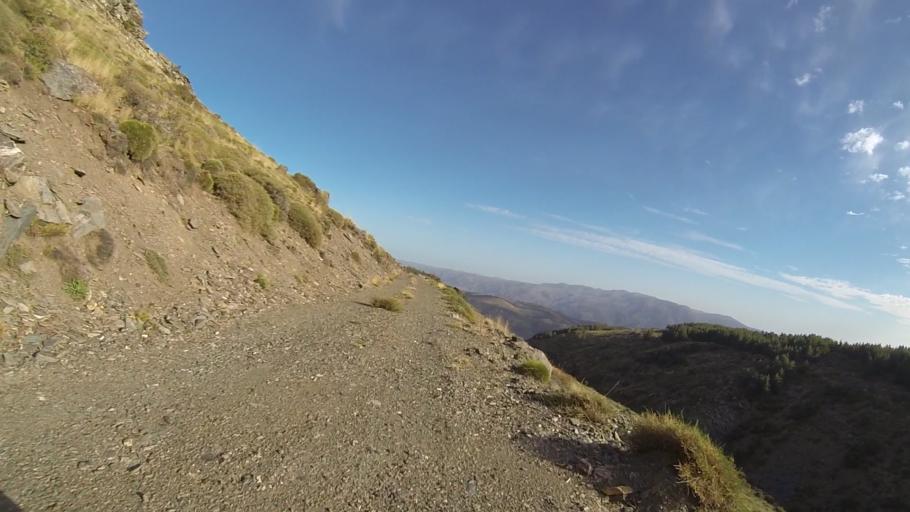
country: ES
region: Andalusia
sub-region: Provincia de Almeria
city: Paterna del Rio
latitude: 37.0757
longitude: -2.8986
